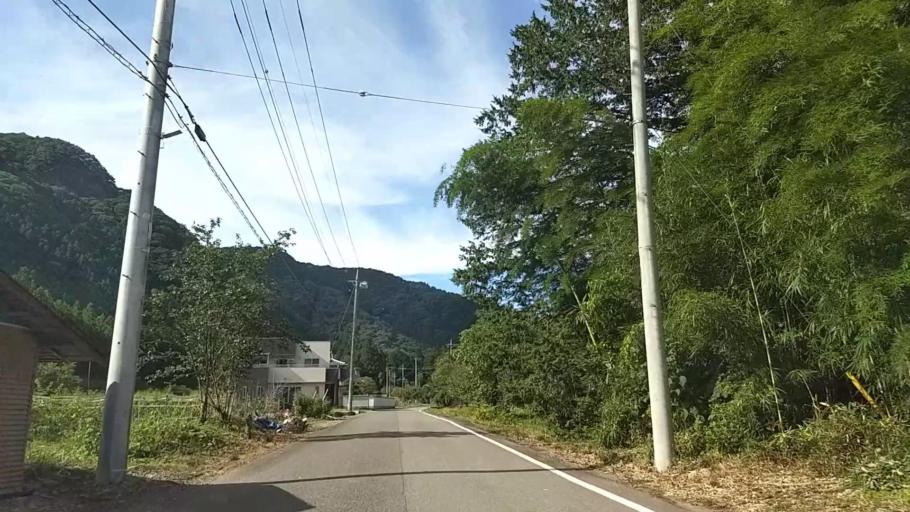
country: JP
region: Tochigi
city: Imaichi
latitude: 36.7854
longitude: 139.6966
